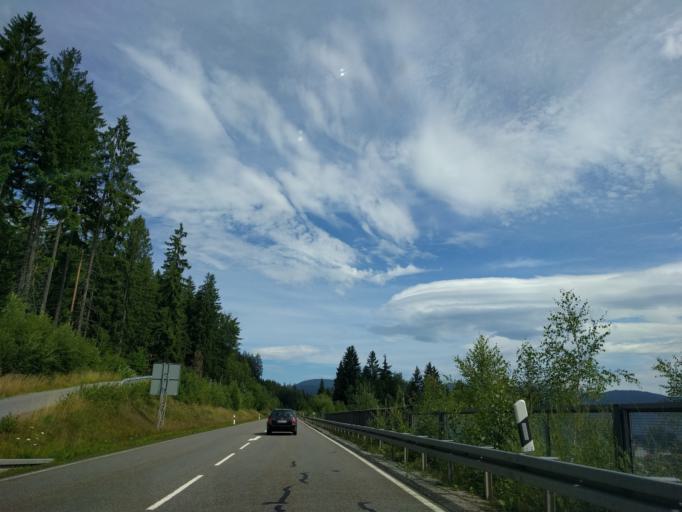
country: DE
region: Bavaria
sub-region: Lower Bavaria
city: Langdorf
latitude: 49.0090
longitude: 13.1431
